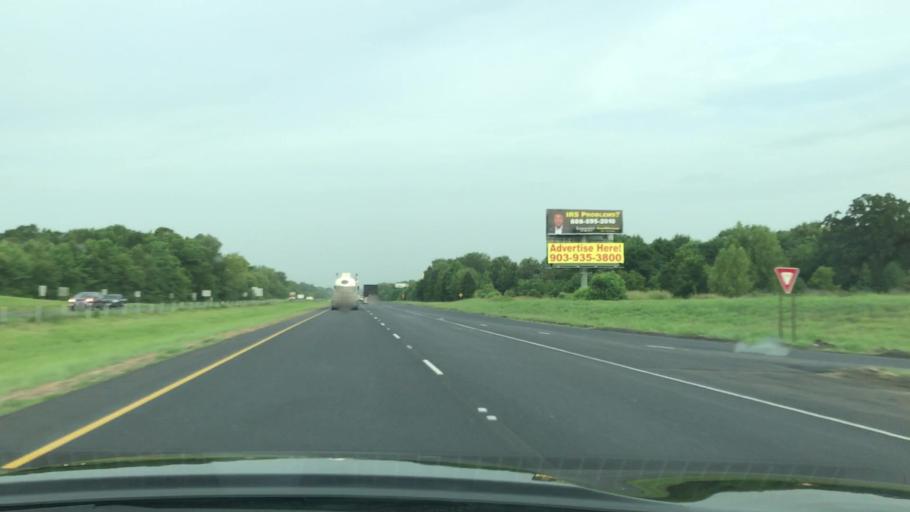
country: US
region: Louisiana
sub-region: Caddo Parish
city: Greenwood
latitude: 32.4446
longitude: -93.9513
